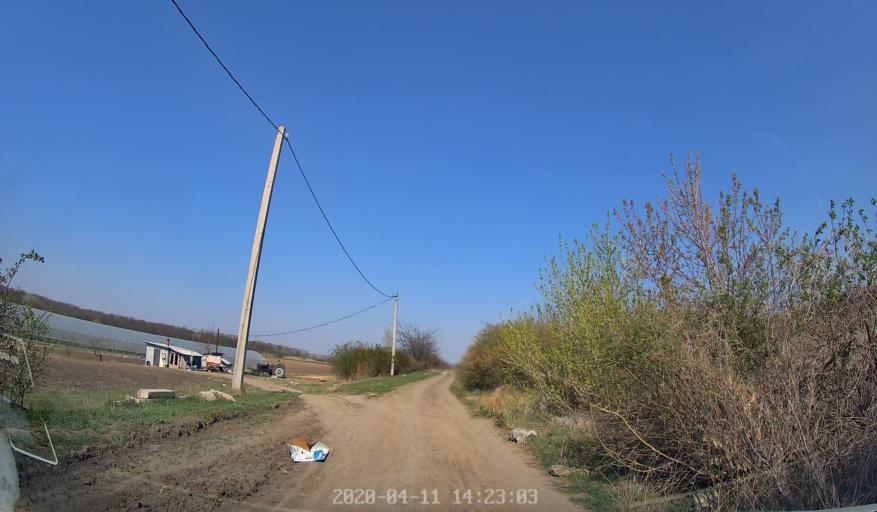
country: MD
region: Chisinau
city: Vadul lui Voda
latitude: 47.0898
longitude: 29.1386
